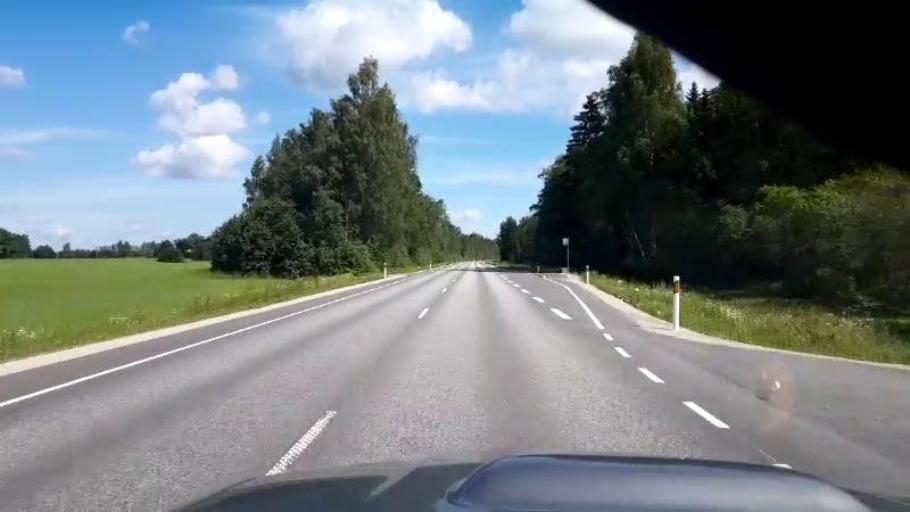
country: EE
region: Jaervamaa
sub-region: Paide linn
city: Paide
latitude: 58.9965
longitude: 25.6759
